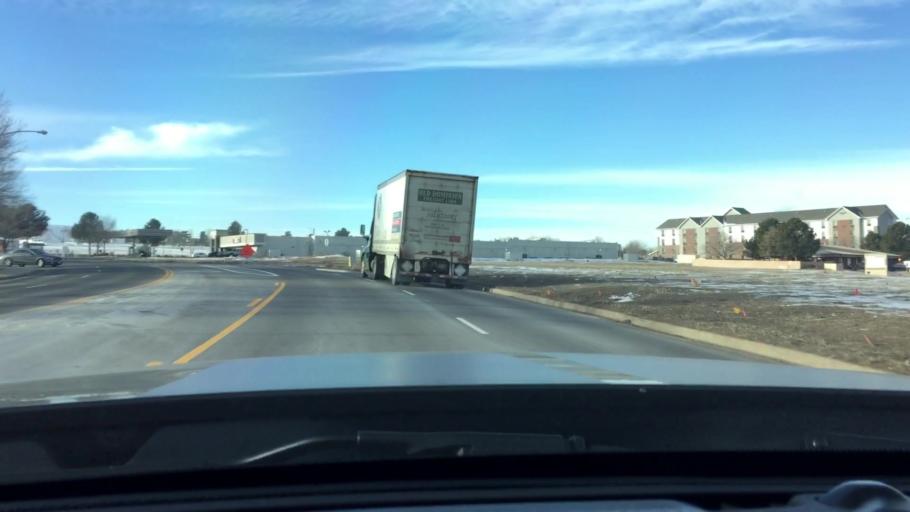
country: US
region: Colorado
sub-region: Adams County
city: Northglenn
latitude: 39.9167
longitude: -105.0057
